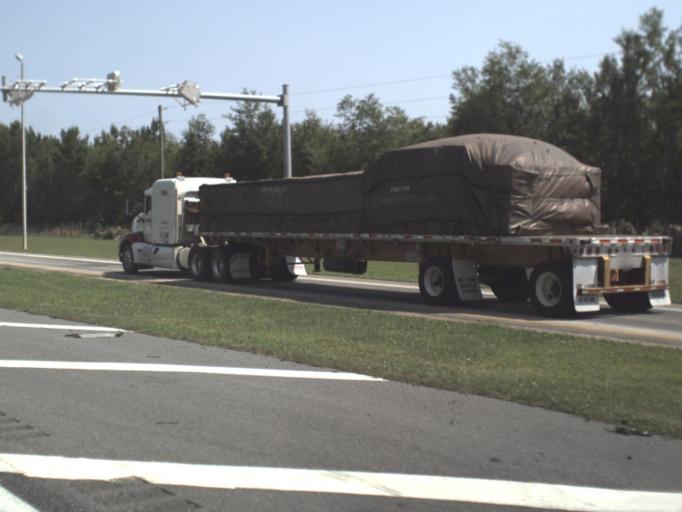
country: US
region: Florida
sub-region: Hamilton County
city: Jasper
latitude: 30.4109
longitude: -82.8932
